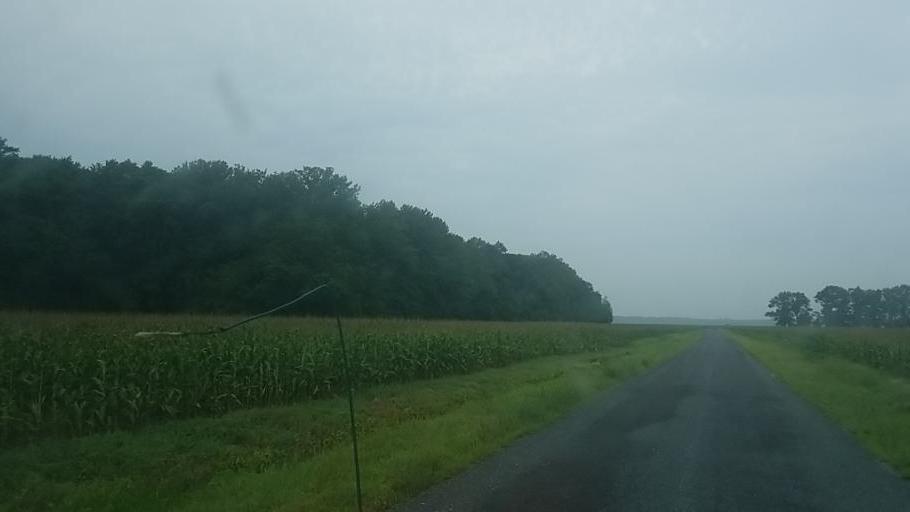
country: US
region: Delaware
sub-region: Sussex County
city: Selbyville
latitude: 38.4365
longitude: -75.2880
